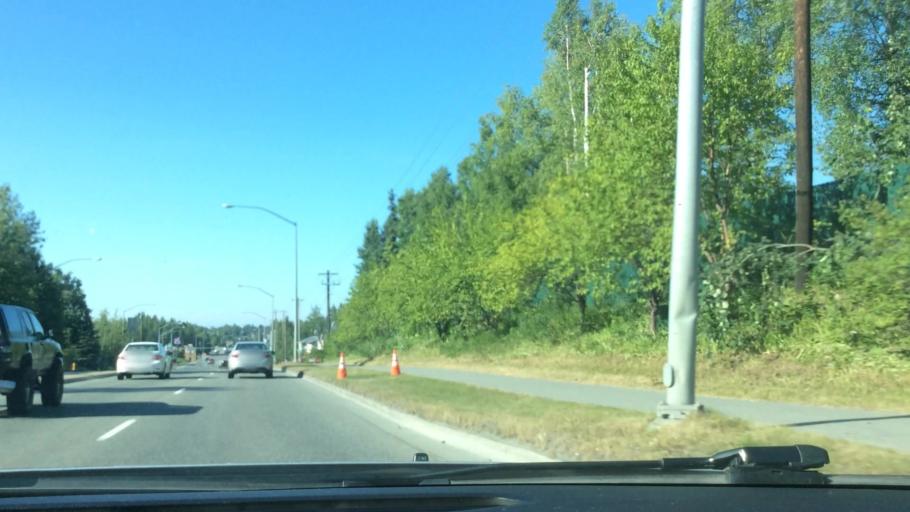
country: US
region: Alaska
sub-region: Anchorage Municipality
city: Anchorage
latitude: 61.1563
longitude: -149.8341
